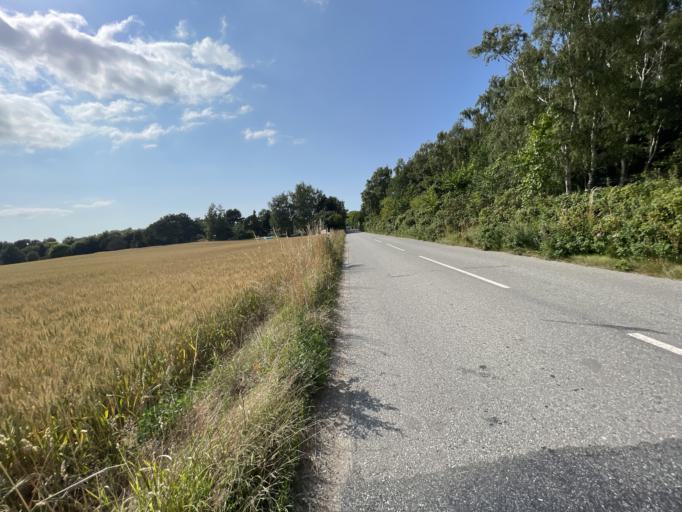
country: DK
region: Capital Region
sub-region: Gribskov Kommune
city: Helsinge
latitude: 56.0900
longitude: 12.1772
